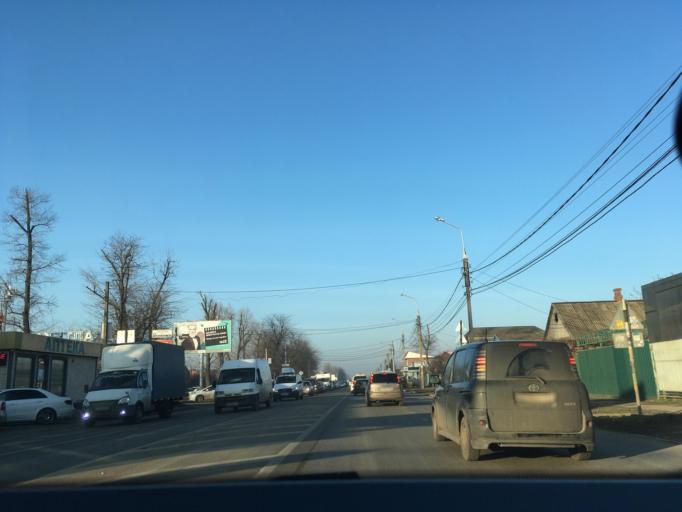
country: RU
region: Krasnodarskiy
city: Krasnodar
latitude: 45.0948
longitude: 39.0137
